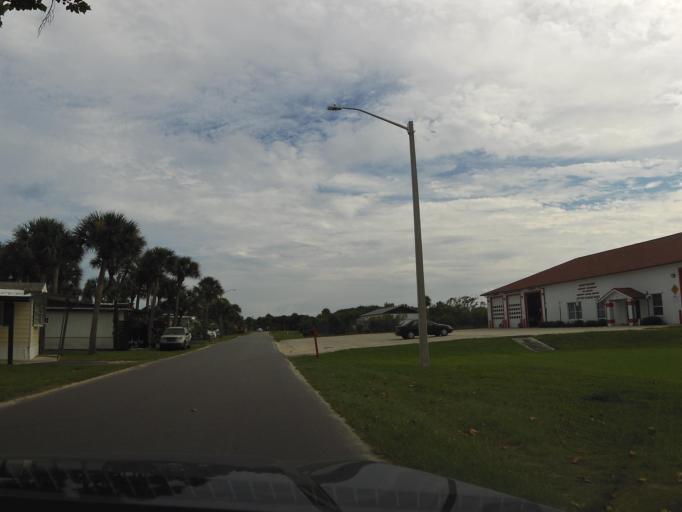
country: US
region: Florida
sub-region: Flagler County
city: Flagler Beach
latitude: 29.4782
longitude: -81.1297
